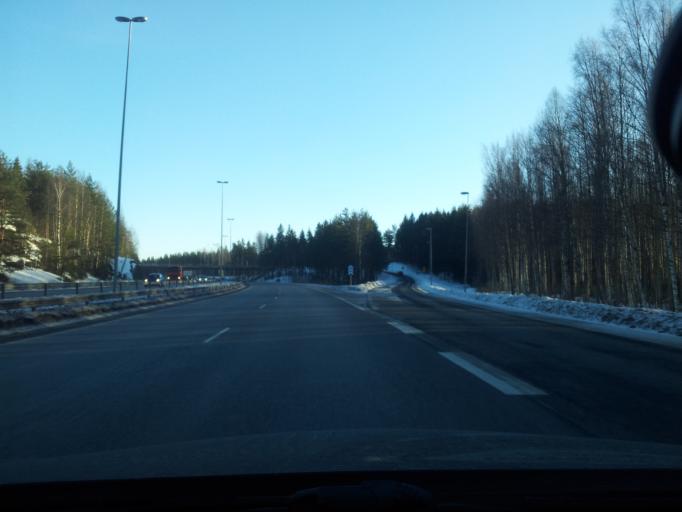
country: FI
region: Uusimaa
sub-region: Helsinki
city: Kirkkonummi
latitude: 60.2760
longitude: 24.4506
